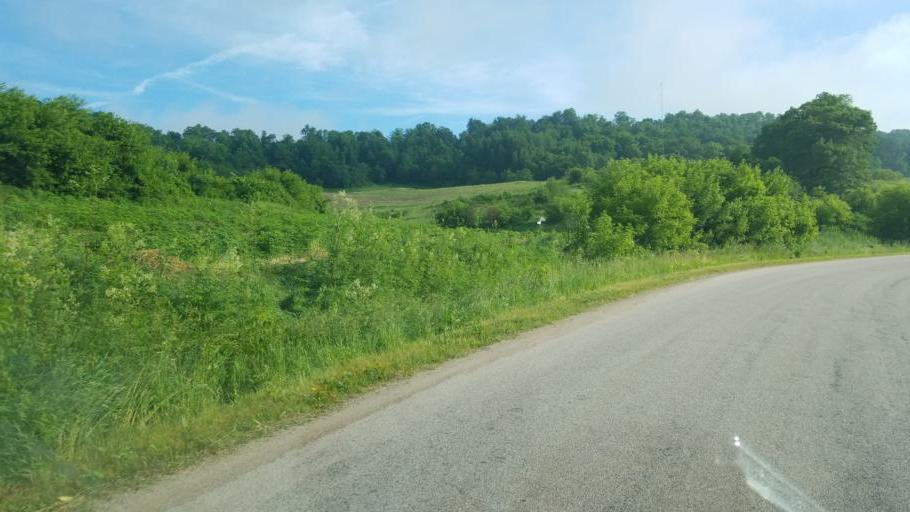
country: US
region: Wisconsin
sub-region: Vernon County
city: Hillsboro
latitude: 43.6070
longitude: -90.3684
